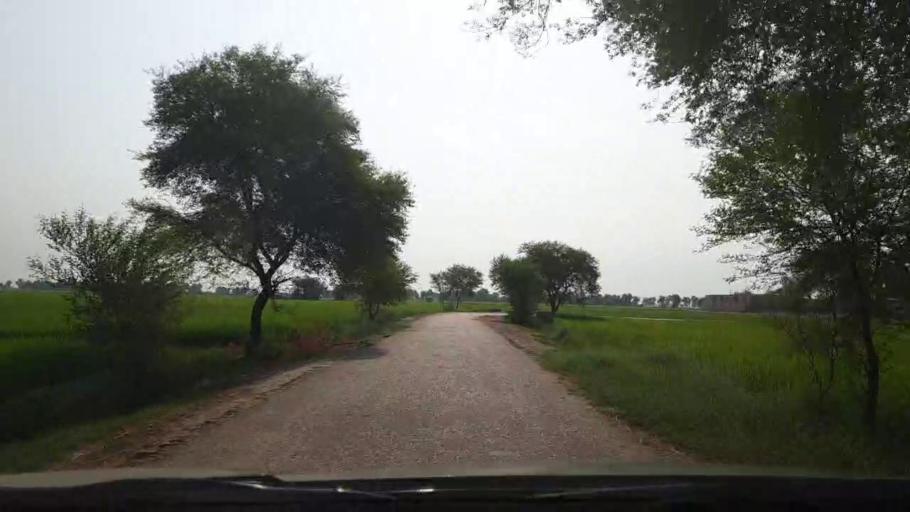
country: PK
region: Sindh
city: Goth Garelo
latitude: 27.4644
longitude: 68.0902
